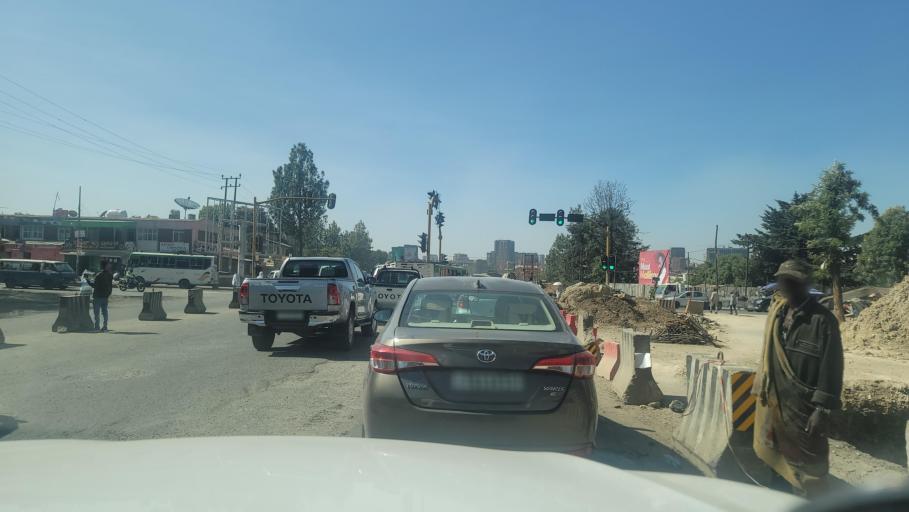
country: ET
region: Adis Abeba
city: Addis Ababa
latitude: 9.0028
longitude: 38.8002
